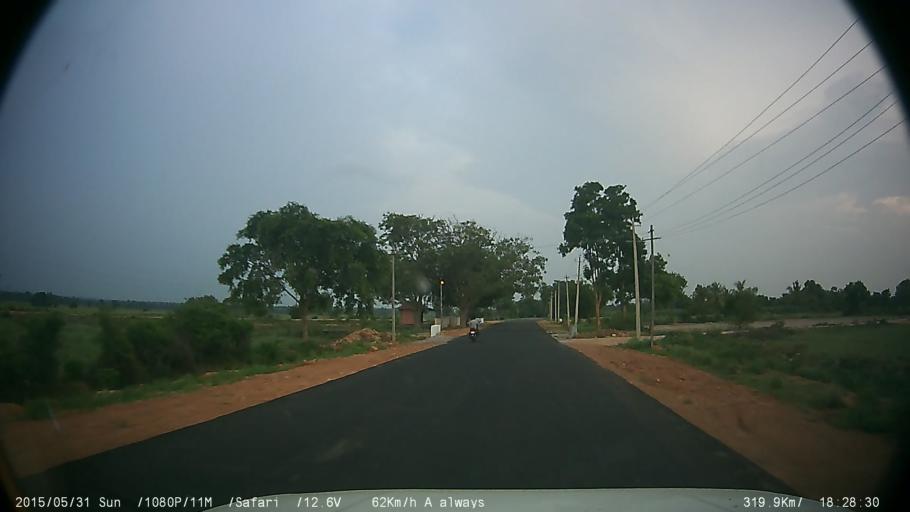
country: IN
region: Karnataka
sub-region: Mysore
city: Nanjangud
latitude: 12.1222
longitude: 76.7228
